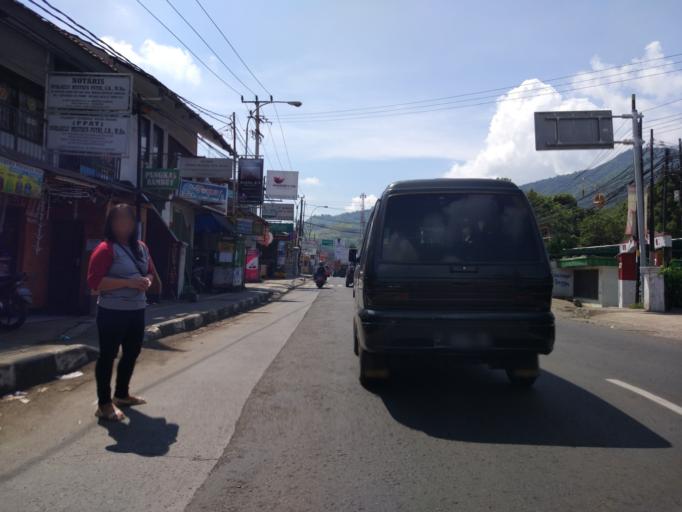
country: ID
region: West Java
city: Cileunyi
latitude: -6.9321
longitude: 107.7777
